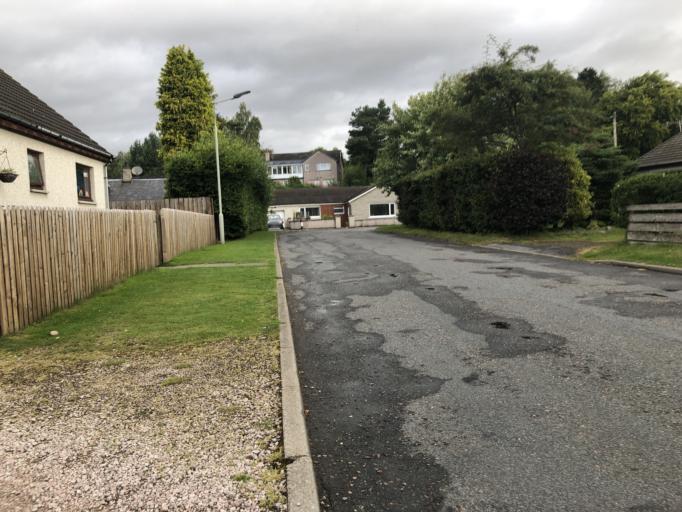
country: GB
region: Scotland
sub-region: Highland
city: Kingussie
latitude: 57.0683
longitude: -4.1120
